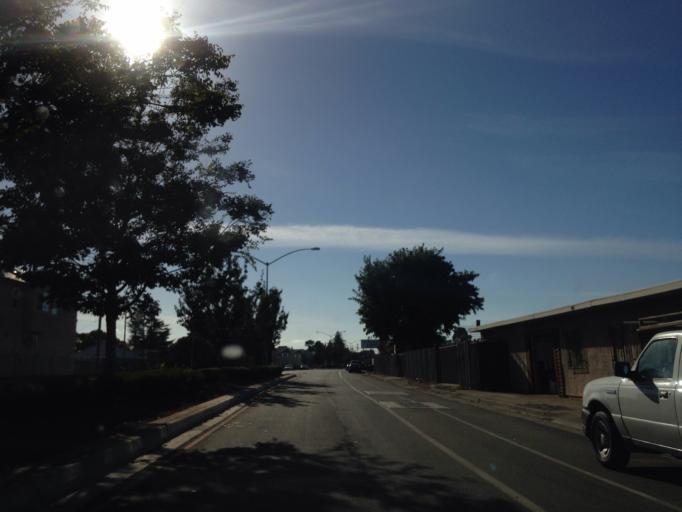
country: US
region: California
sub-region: Contra Costa County
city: Rodeo
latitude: 38.0395
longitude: -122.2647
